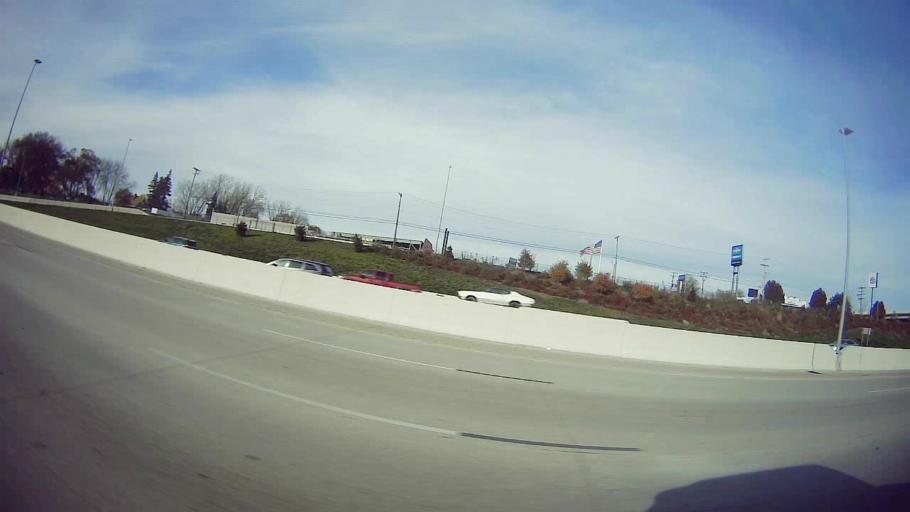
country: US
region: Michigan
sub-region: Wayne County
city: Redford
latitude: 42.3851
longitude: -83.2782
